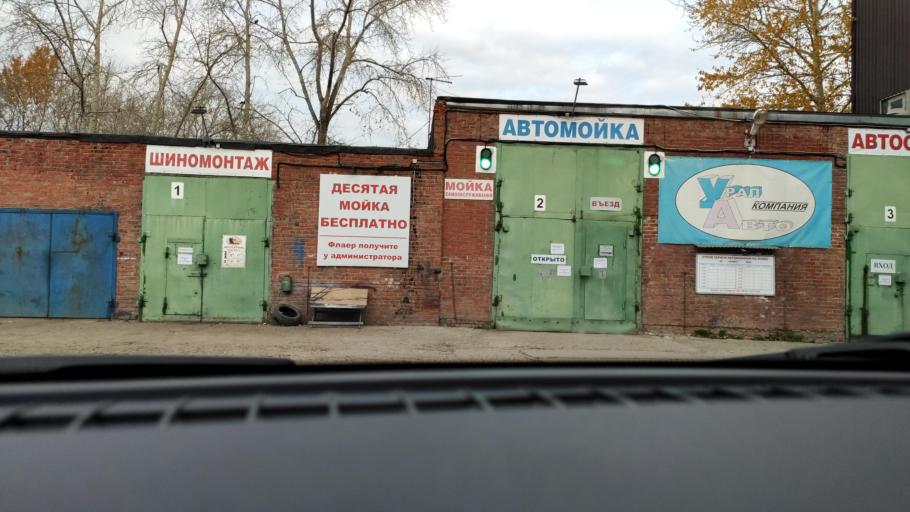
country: RU
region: Perm
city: Kondratovo
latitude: 57.9702
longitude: 56.1830
